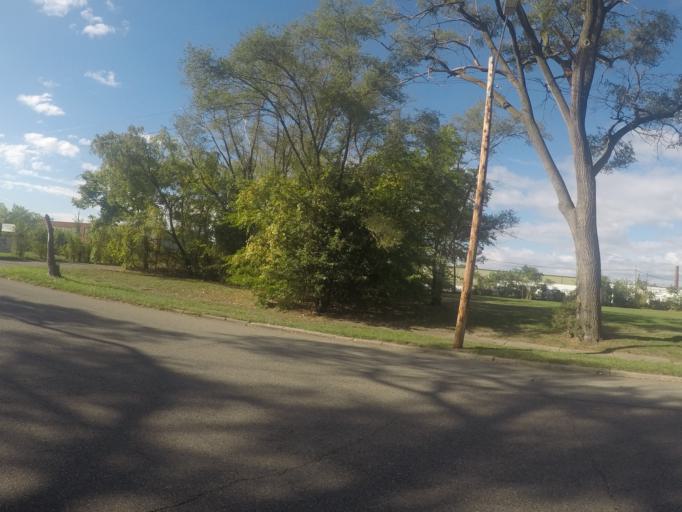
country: US
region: Michigan
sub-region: Wayne County
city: Dearborn
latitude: 42.3592
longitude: -83.1349
